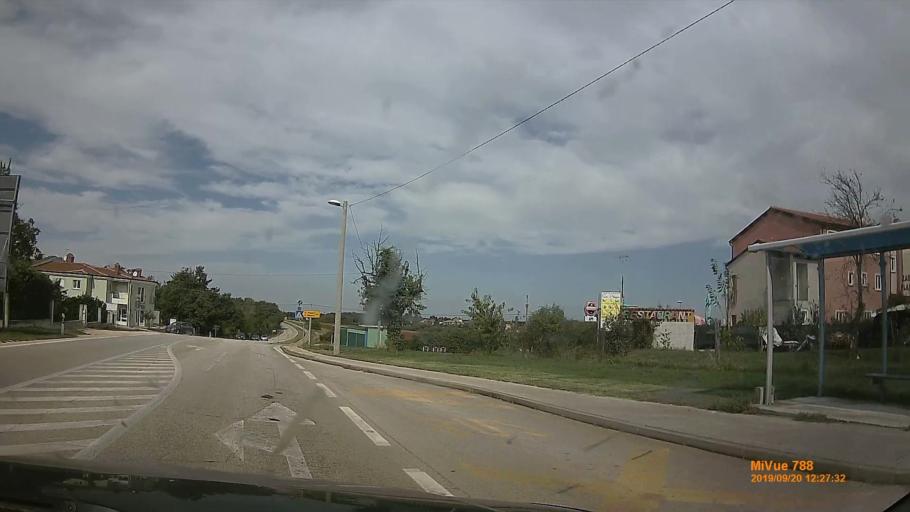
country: HR
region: Istarska
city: Umag
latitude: 45.4078
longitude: 13.5331
